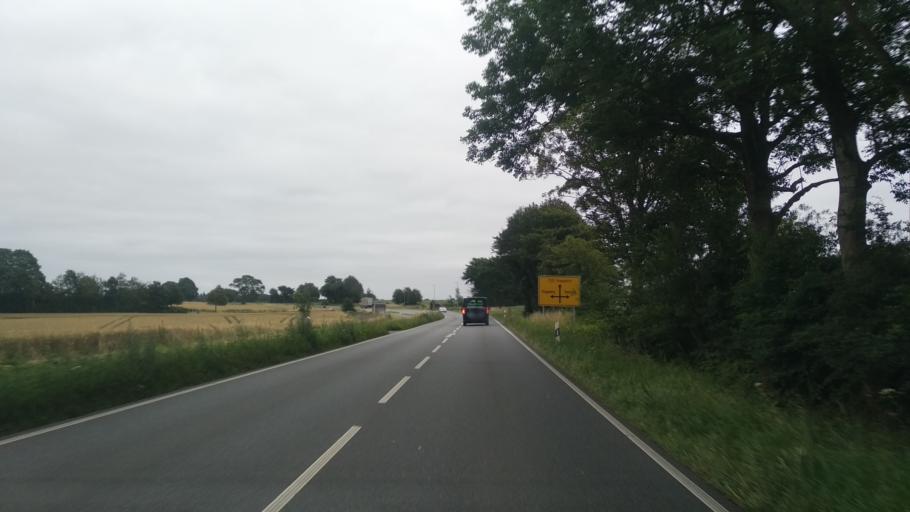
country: DE
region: Schleswig-Holstein
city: Ringsberg
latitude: 54.8041
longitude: 9.5946
